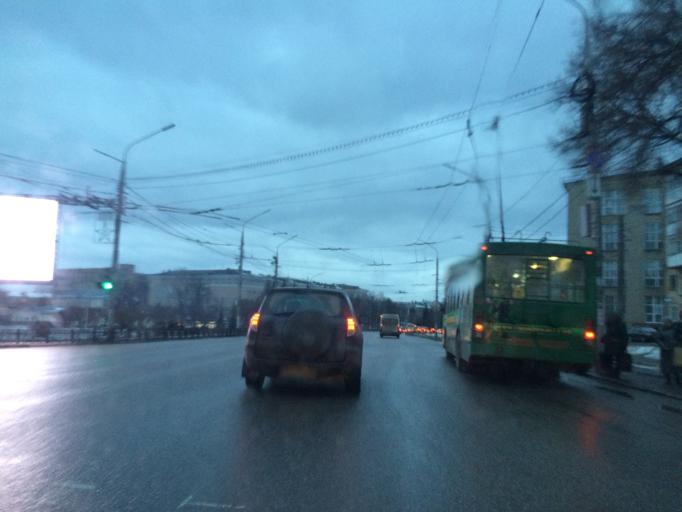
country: RU
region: Tula
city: Mendeleyevskiy
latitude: 54.1639
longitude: 37.5871
